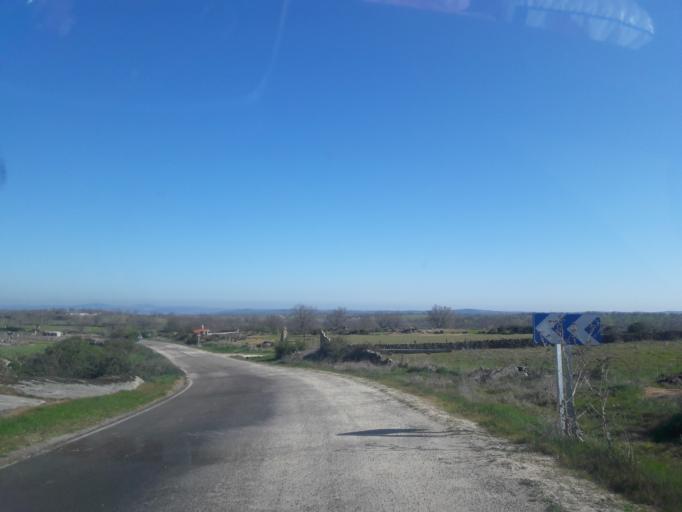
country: ES
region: Castille and Leon
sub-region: Provincia de Salamanca
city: Cabeza del Caballo
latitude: 41.1322
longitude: -6.5543
